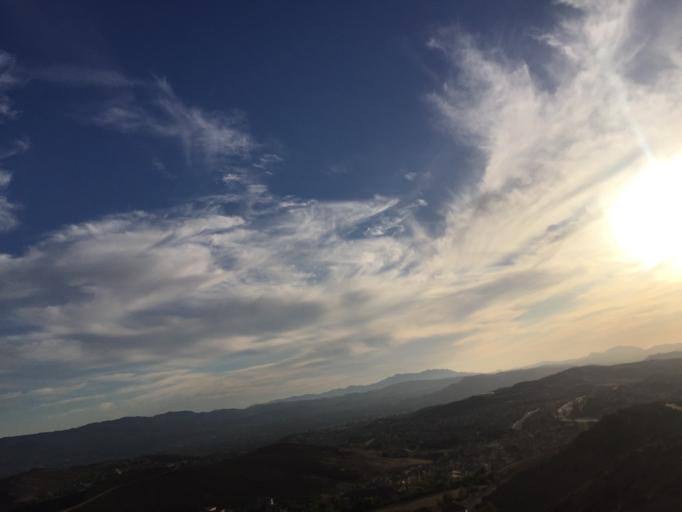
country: US
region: California
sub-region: Ventura County
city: Simi Valley
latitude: 34.3054
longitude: -118.7507
